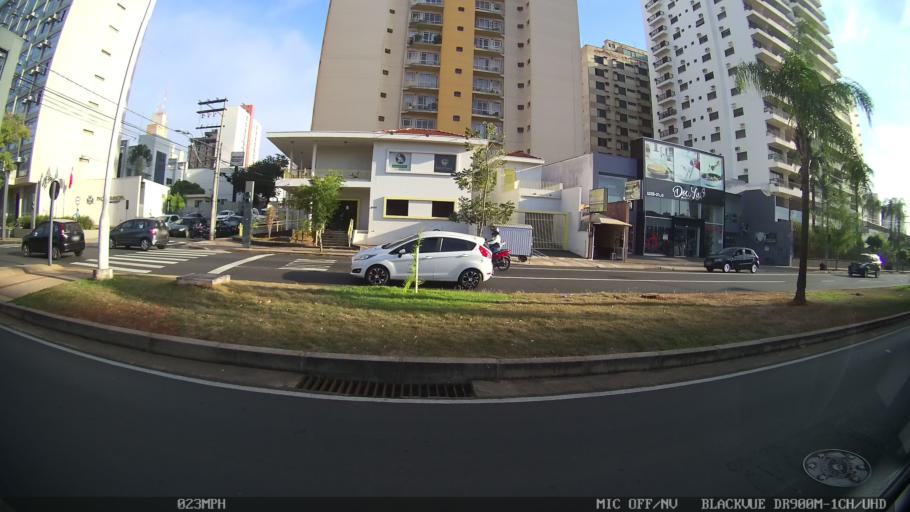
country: BR
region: Sao Paulo
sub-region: Sao Jose Do Rio Preto
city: Sao Jose do Rio Preto
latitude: -20.8136
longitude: -49.3774
